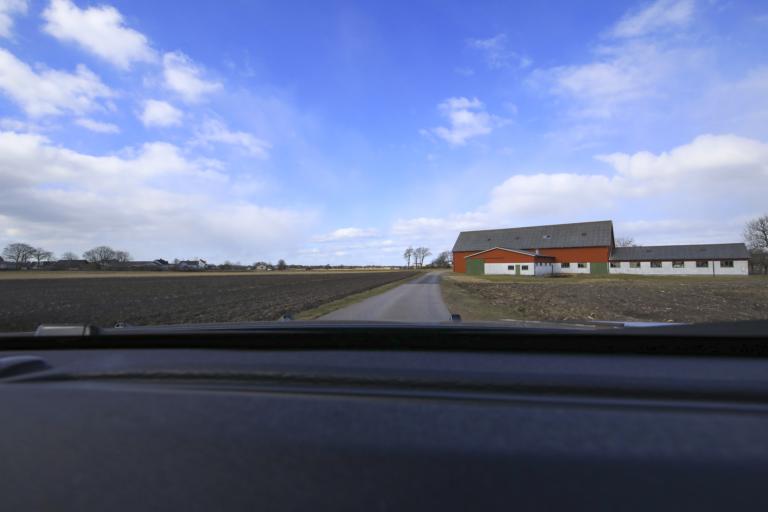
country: SE
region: Halland
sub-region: Kungsbacka Kommun
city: Frillesas
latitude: 57.2338
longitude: 12.1500
